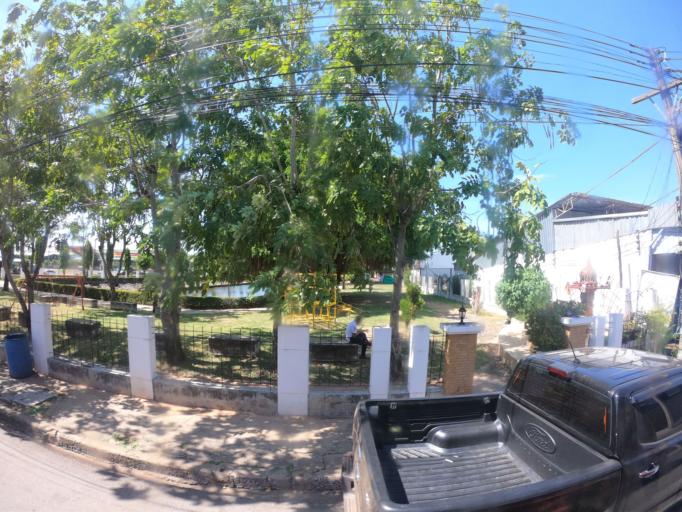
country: TH
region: Khon Kaen
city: Phon
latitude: 15.8130
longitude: 102.6067
